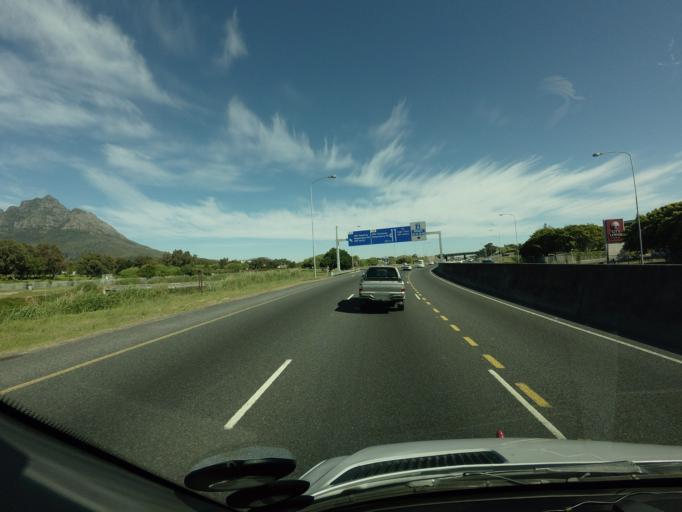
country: ZA
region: Western Cape
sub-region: City of Cape Town
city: Rosebank
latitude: -33.9488
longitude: 18.4900
